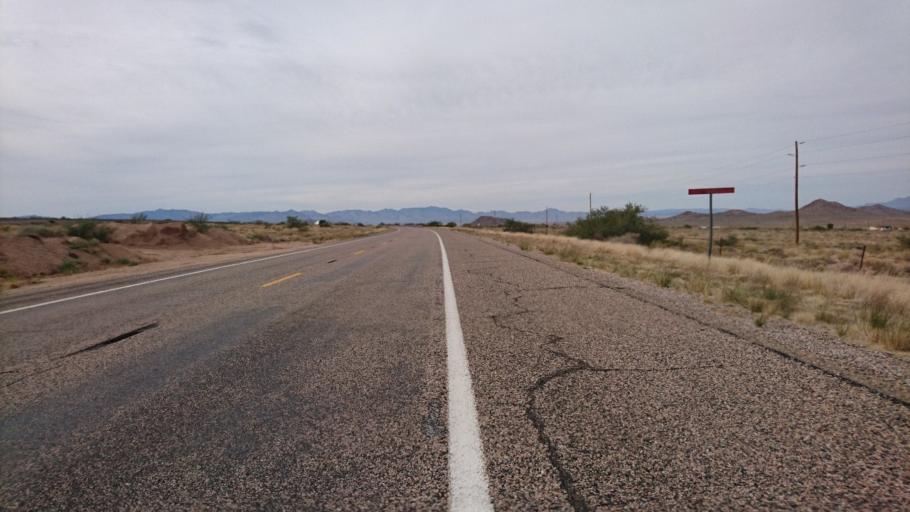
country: US
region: Arizona
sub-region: Mohave County
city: New Kingman-Butler
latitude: 35.4173
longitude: -113.7955
